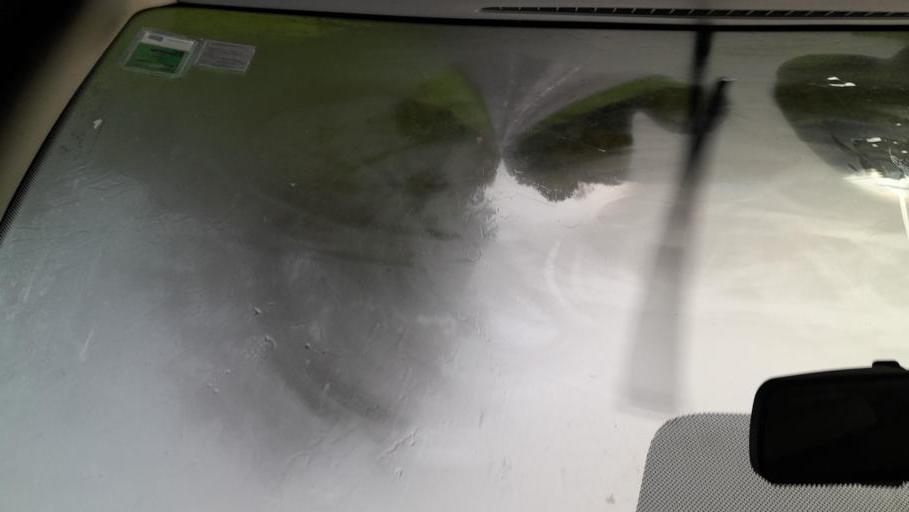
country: FR
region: Pays de la Loire
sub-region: Departement de la Mayenne
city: Ballots
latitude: 47.8735
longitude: -1.0468
